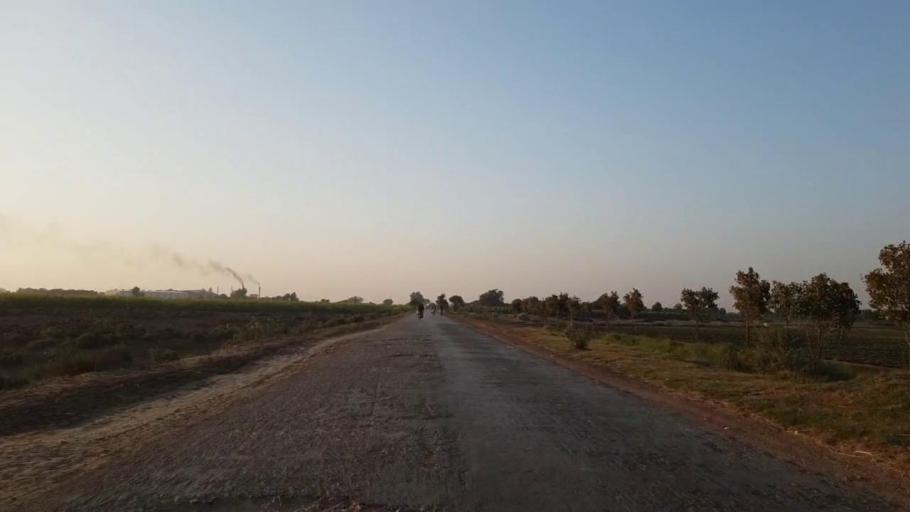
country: PK
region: Sindh
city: Chambar
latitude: 25.2452
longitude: 68.6846
